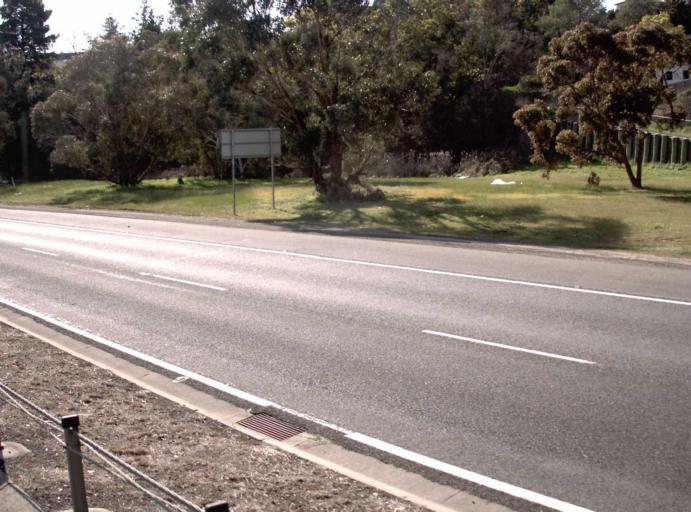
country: AU
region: Tasmania
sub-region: Launceston
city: Newnham
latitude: -41.4071
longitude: 147.1240
